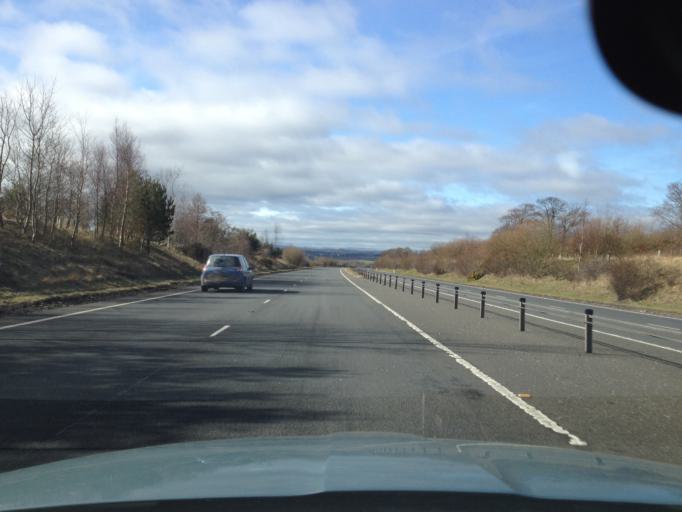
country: GB
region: Scotland
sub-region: East Lothian
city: East Linton
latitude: 55.9771
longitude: -2.6957
